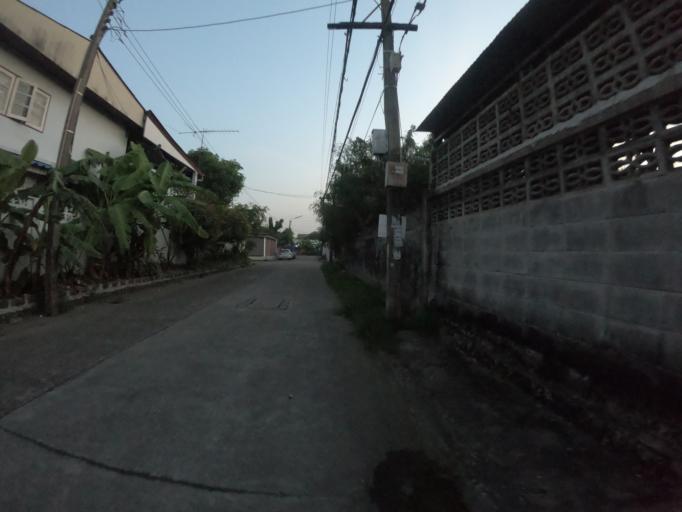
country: TH
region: Bangkok
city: Lat Phrao
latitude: 13.8239
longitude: 100.6081
